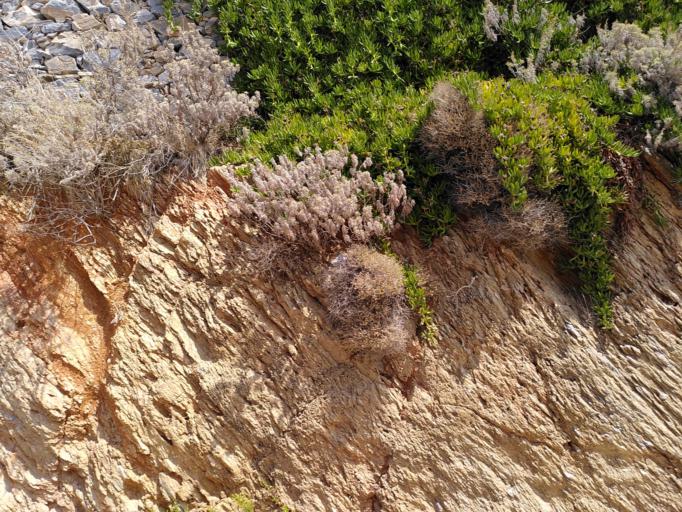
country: GR
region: South Aegean
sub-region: Nomos Kykladon
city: Amorgos
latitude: 36.9090
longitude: 25.9736
